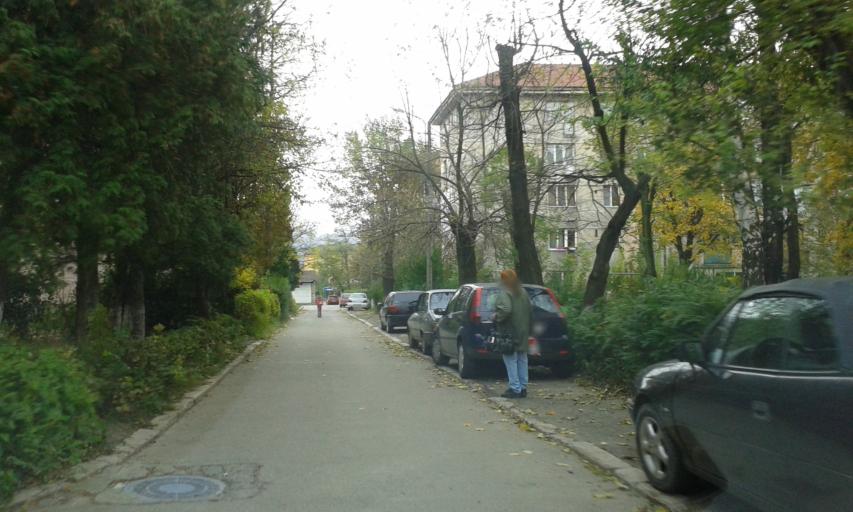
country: RO
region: Hunedoara
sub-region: Municipiul Petrosani
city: Petrosani
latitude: 45.4045
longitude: 23.3732
